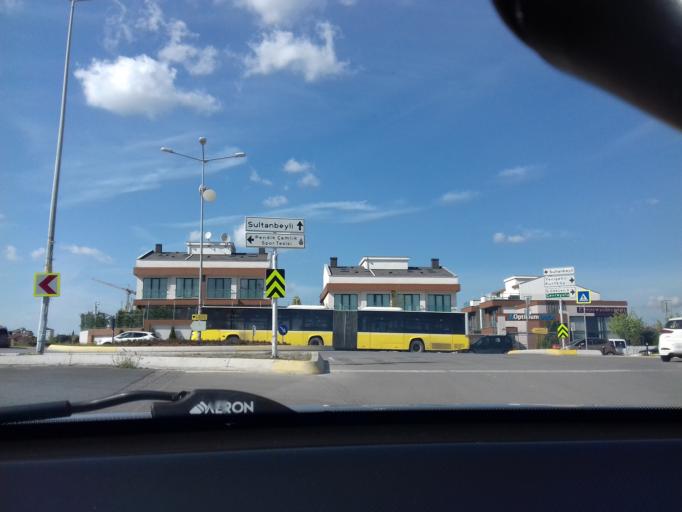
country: TR
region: Istanbul
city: Sultanbeyli
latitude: 40.9296
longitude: 29.2836
